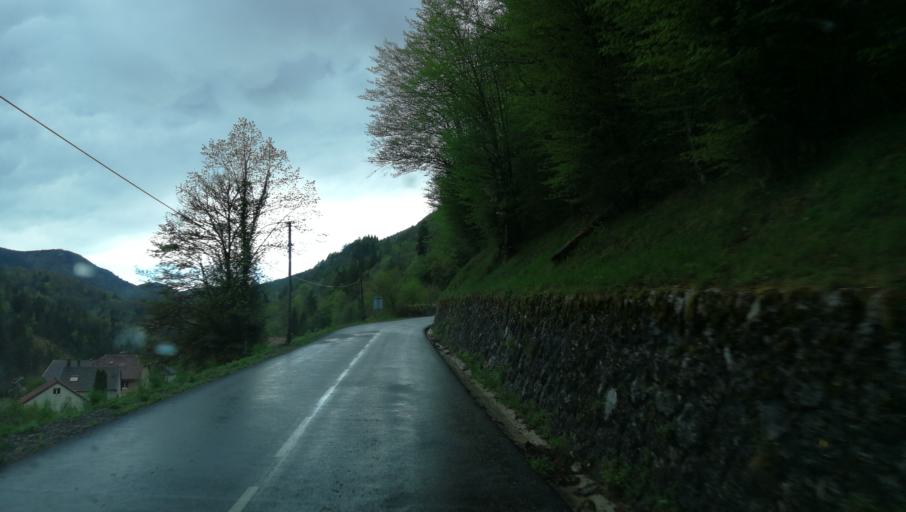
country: FR
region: Franche-Comte
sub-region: Departement du Jura
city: Saint-Claude
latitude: 46.3692
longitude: 5.8655
